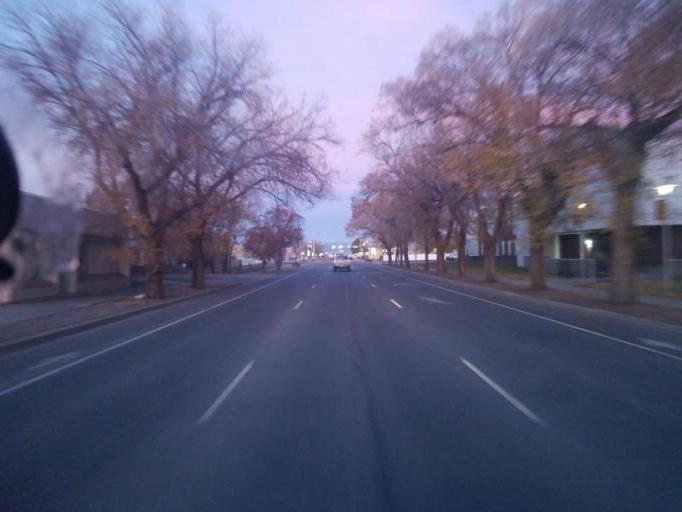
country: US
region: Colorado
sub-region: Alamosa County
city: Alamosa
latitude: 37.4682
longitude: -105.8716
